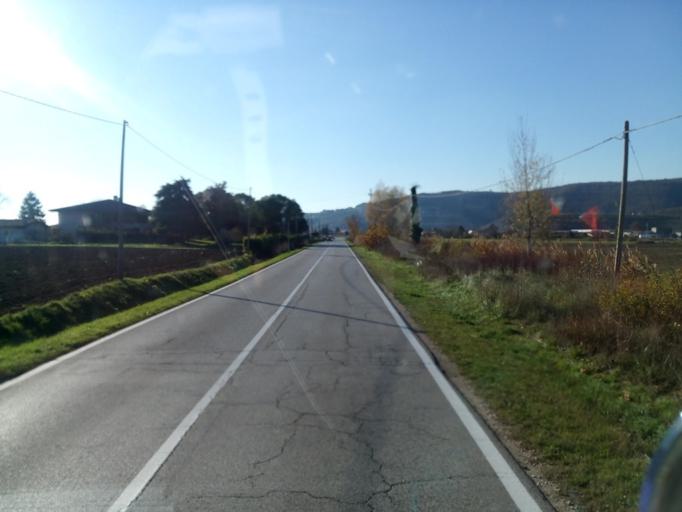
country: IT
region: Veneto
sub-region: Provincia di Vicenza
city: Villaga
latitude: 45.3772
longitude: 11.5336
